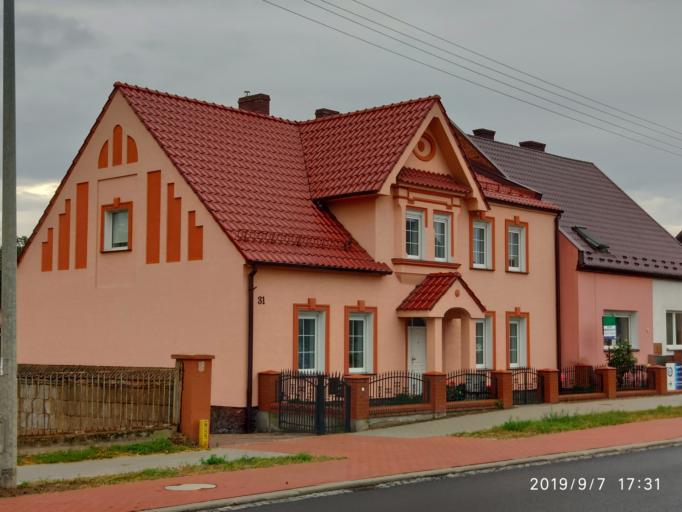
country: PL
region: Lubusz
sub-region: Powiat slubicki
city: Cybinka
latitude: 52.1965
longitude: 14.7893
